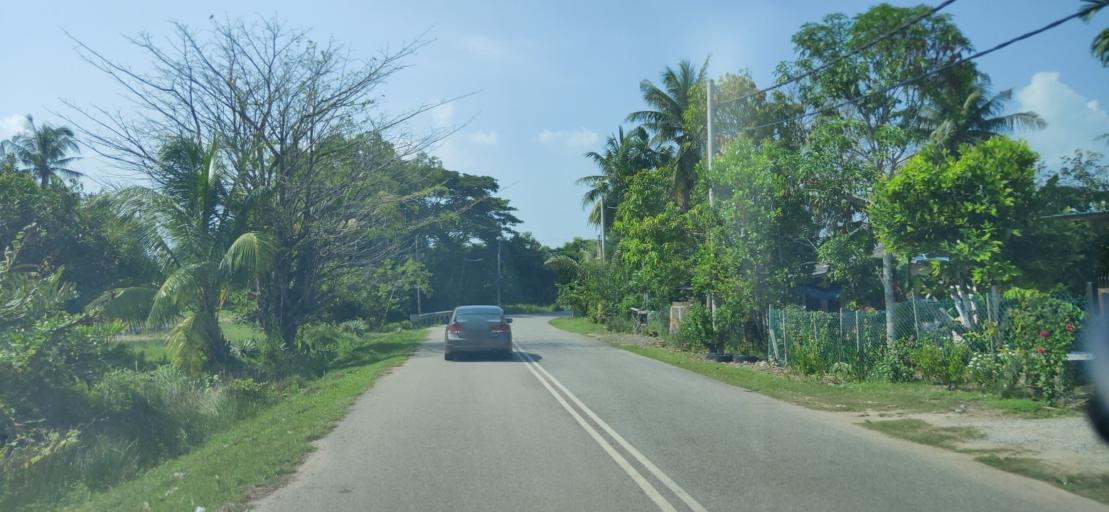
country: MY
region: Kedah
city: Sungai Petani
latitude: 5.6548
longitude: 100.4627
